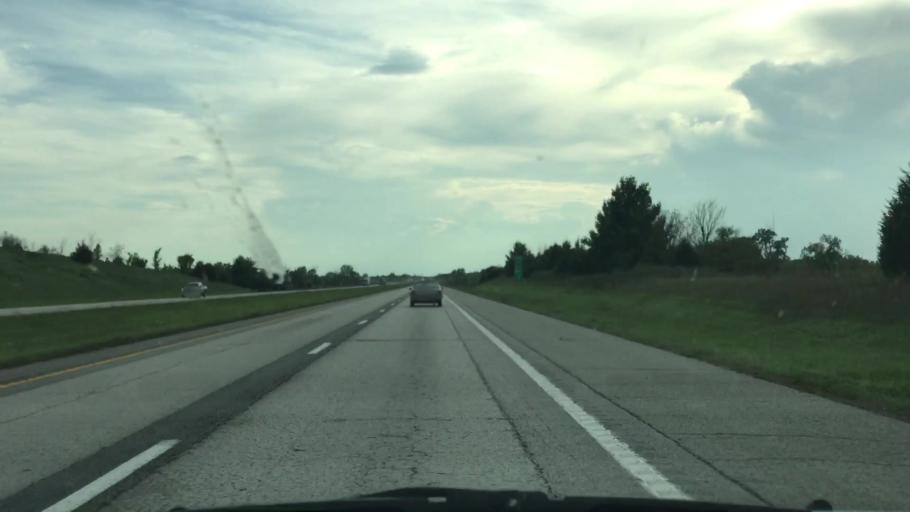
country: US
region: Missouri
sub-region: Harrison County
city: Bethany
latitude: 40.1666
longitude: -94.0247
